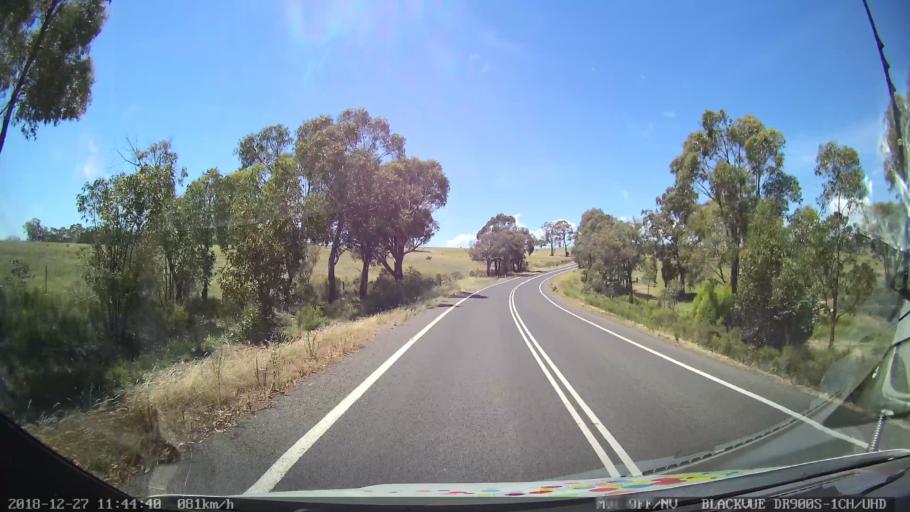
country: AU
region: New South Wales
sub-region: Bathurst Regional
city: Perthville
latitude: -33.5749
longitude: 149.4759
